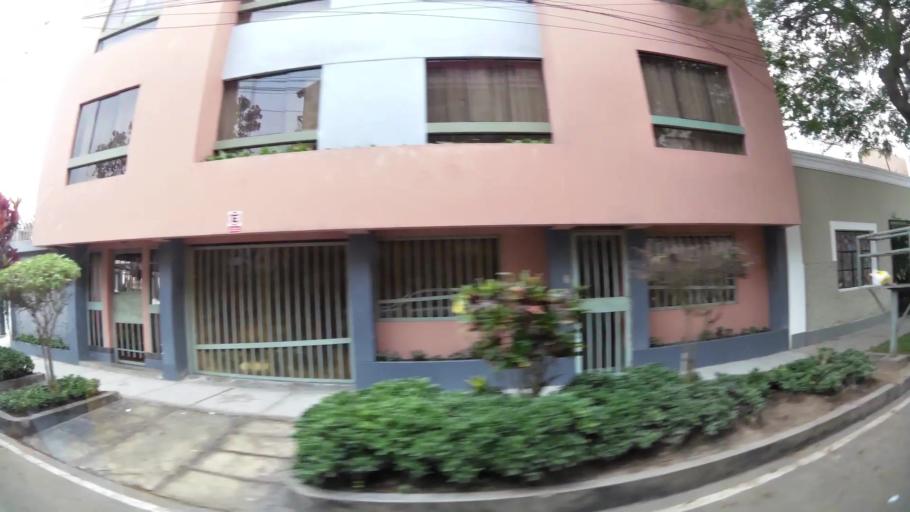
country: PE
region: Lima
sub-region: Lima
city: Surco
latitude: -12.1392
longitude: -77.0212
